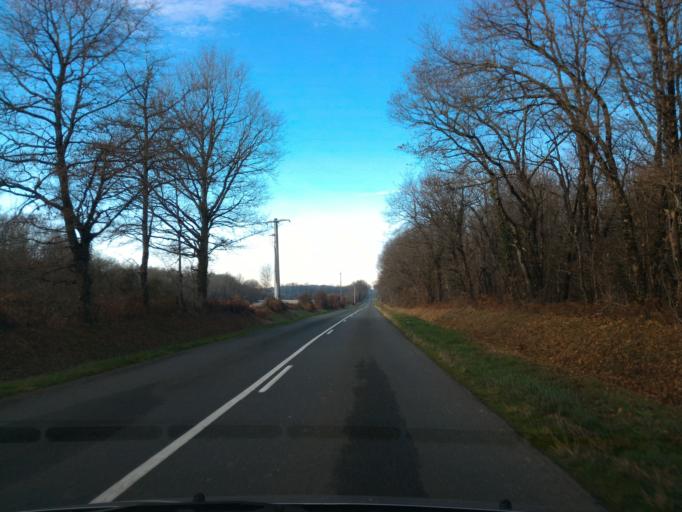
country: FR
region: Poitou-Charentes
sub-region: Departement de la Charente
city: Confolens
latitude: 46.0338
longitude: 0.6116
